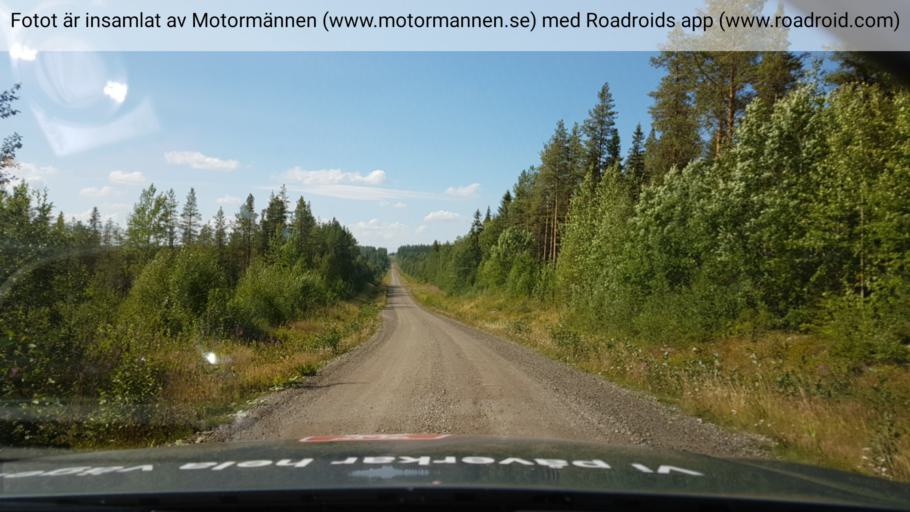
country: SE
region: Vaesterbotten
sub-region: Dorotea Kommun
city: Dorotea
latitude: 64.0887
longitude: 16.5311
